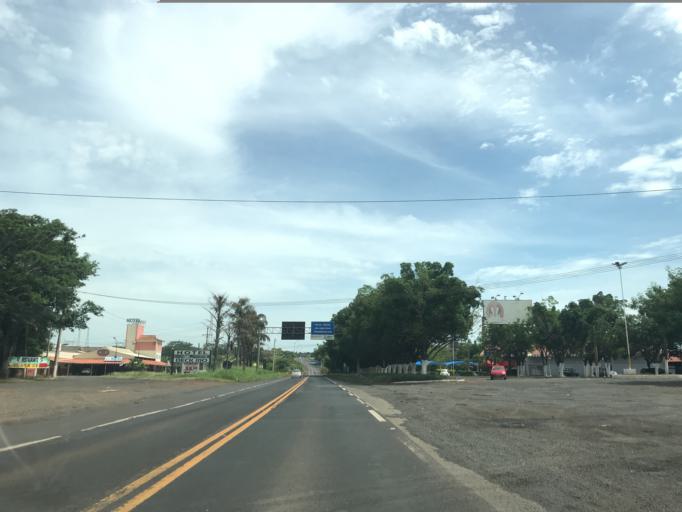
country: BR
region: Sao Paulo
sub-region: Nova Granada
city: Nova Granada
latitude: -20.3081
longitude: -49.2080
